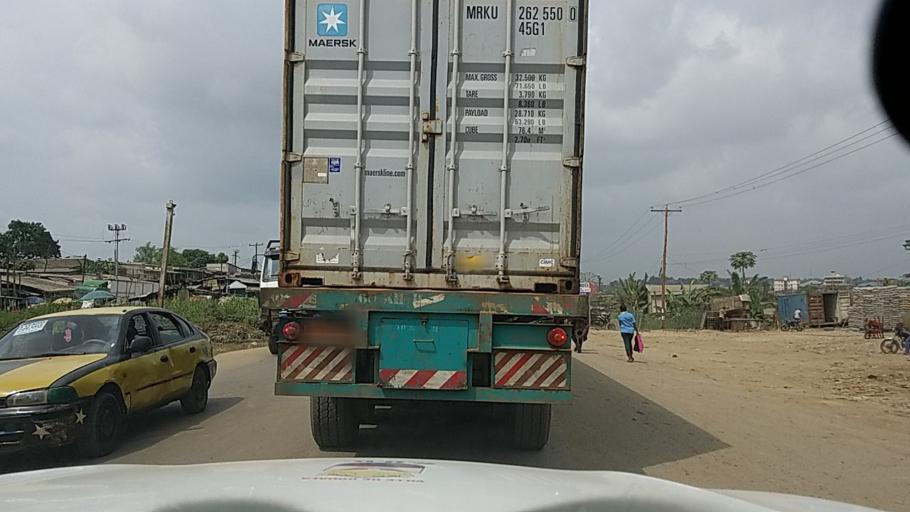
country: CM
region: Littoral
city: Douala
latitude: 3.9952
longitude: 9.7836
